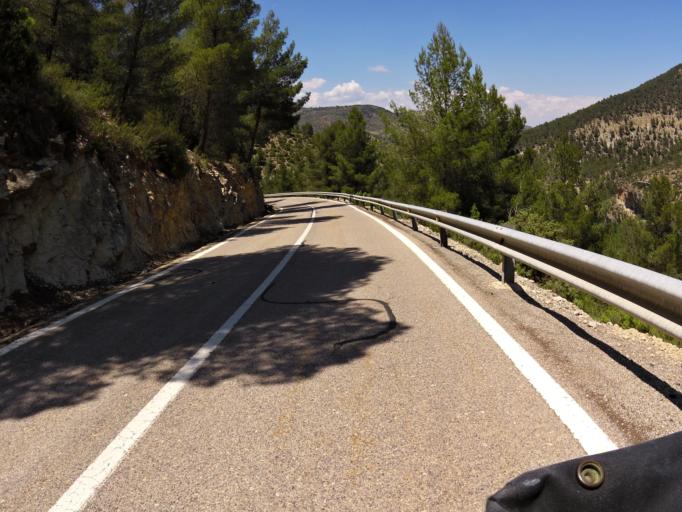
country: ES
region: Castille-La Mancha
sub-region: Provincia de Cuenca
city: Santa Cruz de Moya
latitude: 39.9823
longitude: -1.2755
